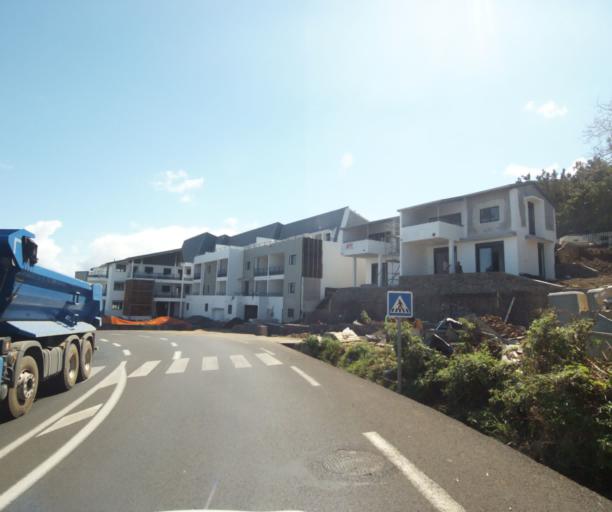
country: RE
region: Reunion
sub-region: Reunion
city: La Possession
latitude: -20.9854
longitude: 55.3338
